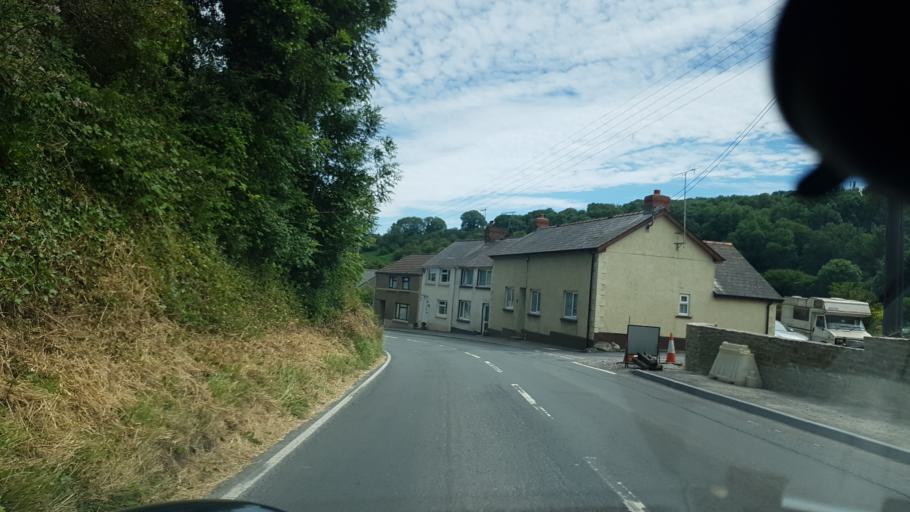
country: GB
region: Wales
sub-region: Carmarthenshire
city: Saint Clears
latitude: 51.7662
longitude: -4.4653
